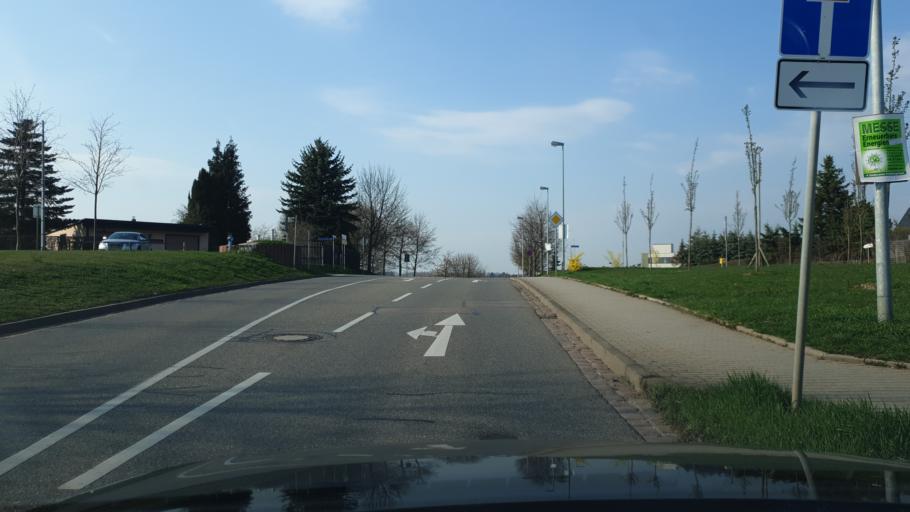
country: DE
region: Saxony
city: Mittweida
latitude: 50.9809
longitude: 12.9711
